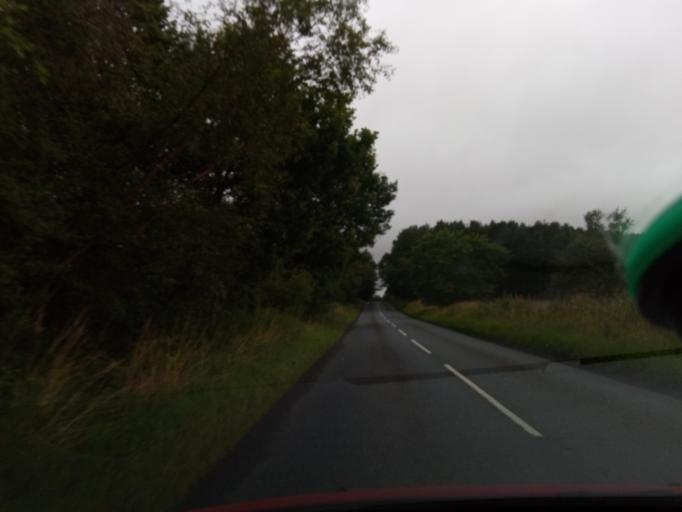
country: GB
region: Scotland
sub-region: The Scottish Borders
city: Saint Boswells
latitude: 55.6552
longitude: -2.5503
